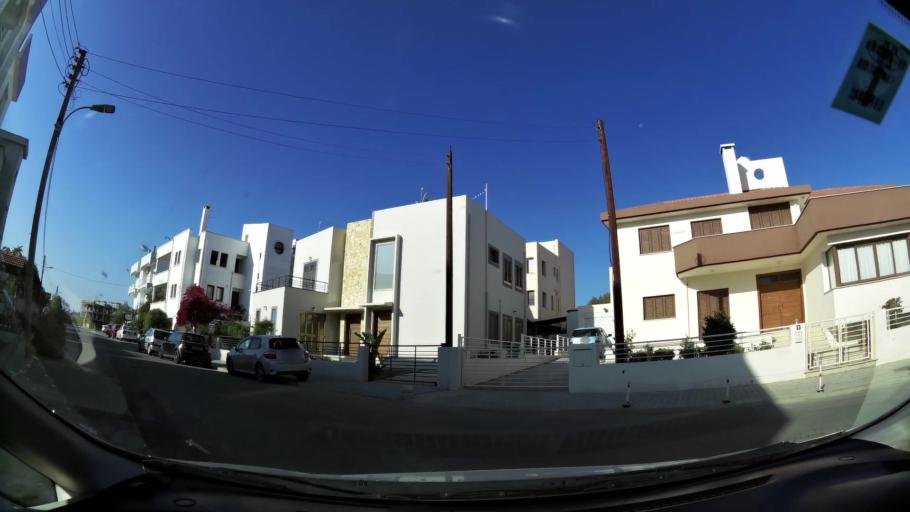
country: CY
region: Lefkosia
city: Nicosia
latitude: 35.2139
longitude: 33.2981
